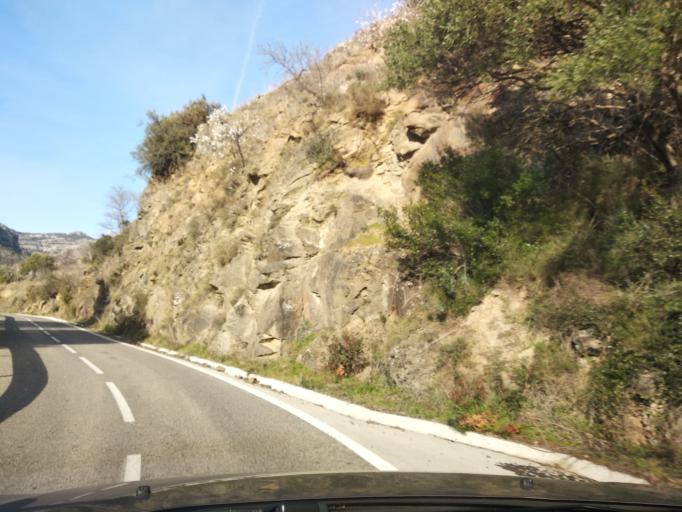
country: ES
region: Catalonia
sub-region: Provincia de Tarragona
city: Margalef
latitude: 41.2322
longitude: 0.7812
